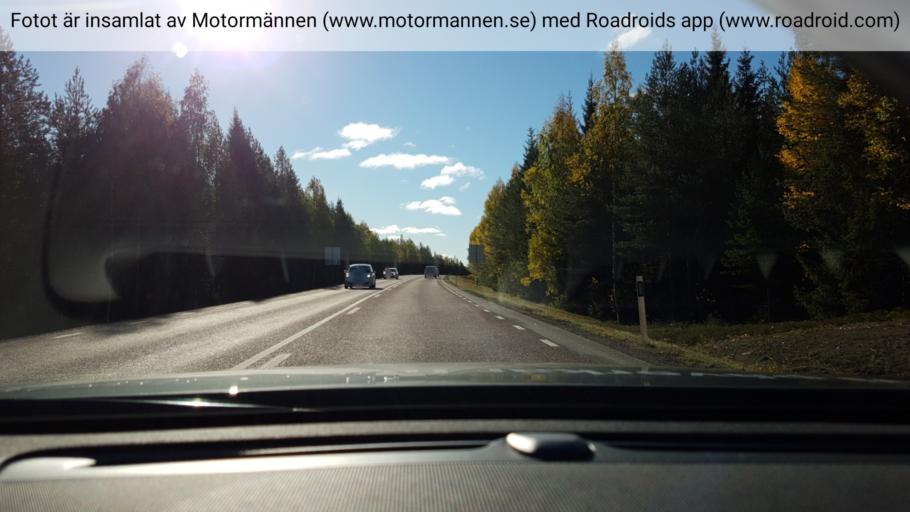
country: SE
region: Vaesterbotten
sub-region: Skelleftea Kommun
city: Burea
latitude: 64.6296
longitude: 21.1784
